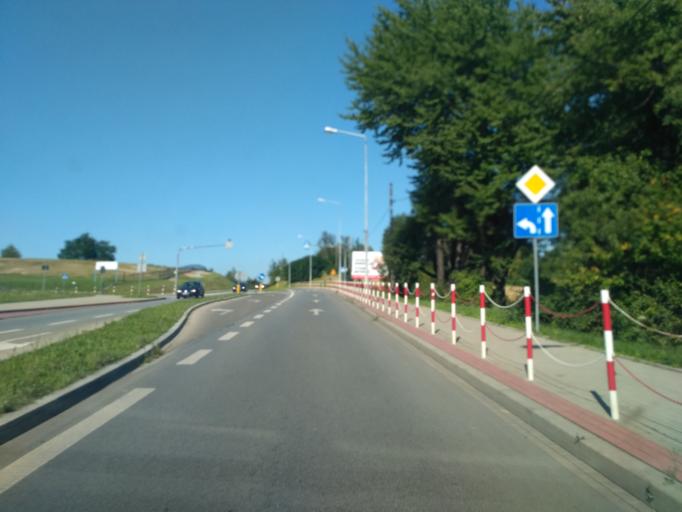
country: PL
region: Subcarpathian Voivodeship
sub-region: Krosno
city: Krosno
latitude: 49.6975
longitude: 21.7835
